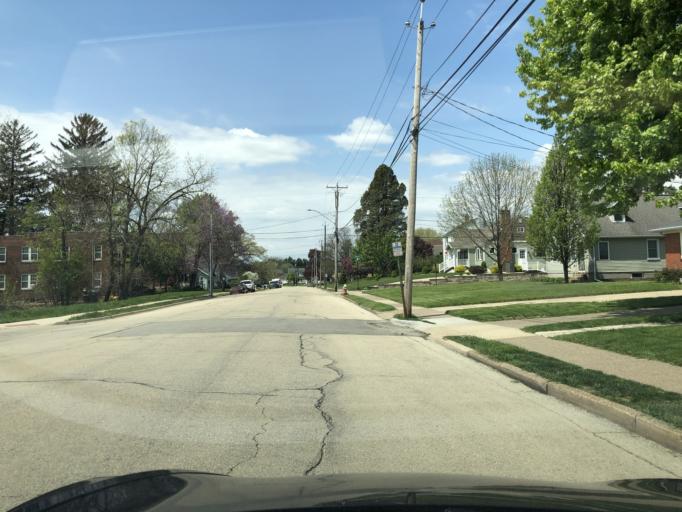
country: US
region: Iowa
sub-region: Dubuque County
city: Dubuque
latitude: 42.4788
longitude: -90.6626
